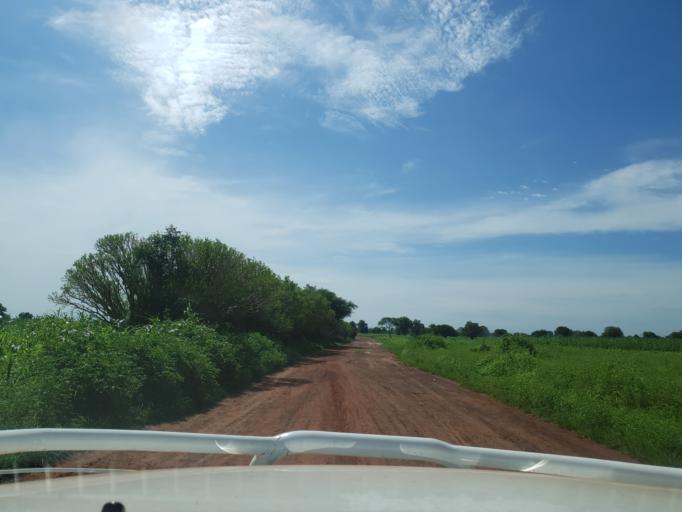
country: ML
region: Koulikoro
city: Banamba
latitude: 13.2778
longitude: -7.5484
